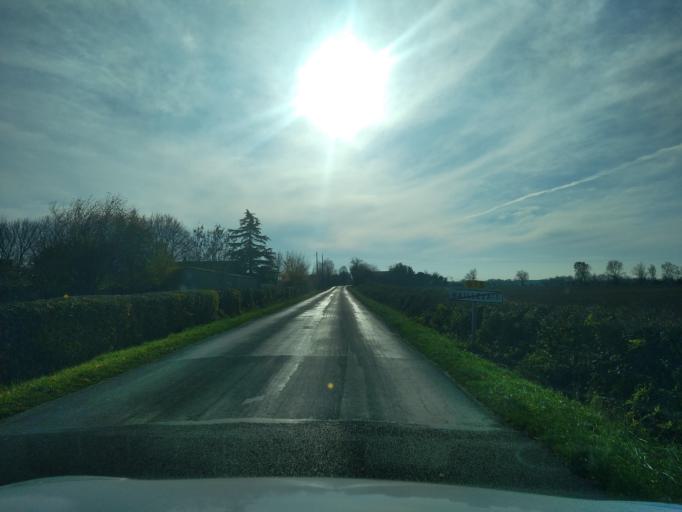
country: FR
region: Pays de la Loire
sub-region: Departement de la Vendee
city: Maillezais
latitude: 46.3657
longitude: -0.7421
